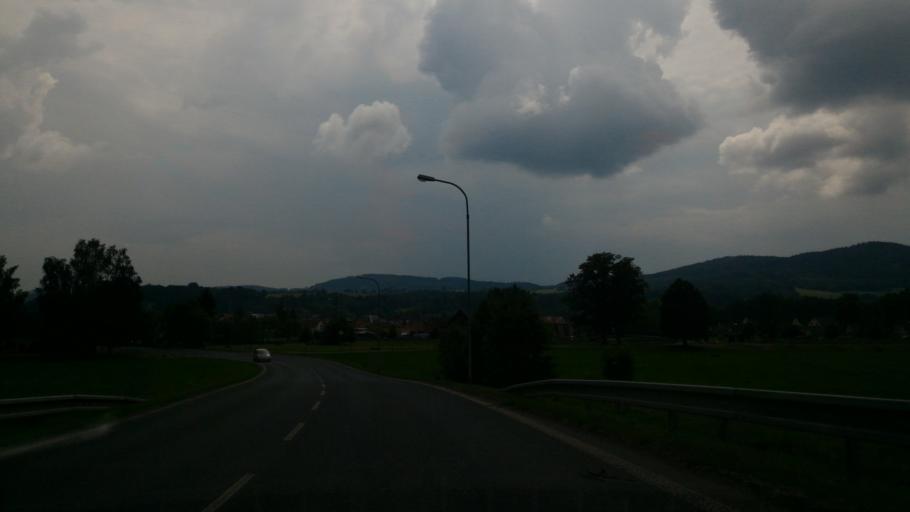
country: CZ
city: Hradek nad Nisou
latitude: 50.8538
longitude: 14.8380
